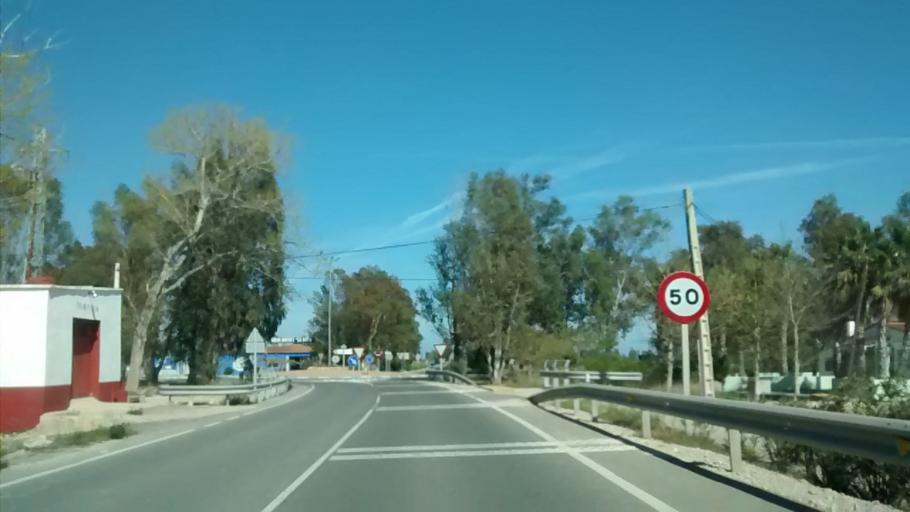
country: ES
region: Catalonia
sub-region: Provincia de Tarragona
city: Deltebre
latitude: 40.7140
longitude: 0.8269
